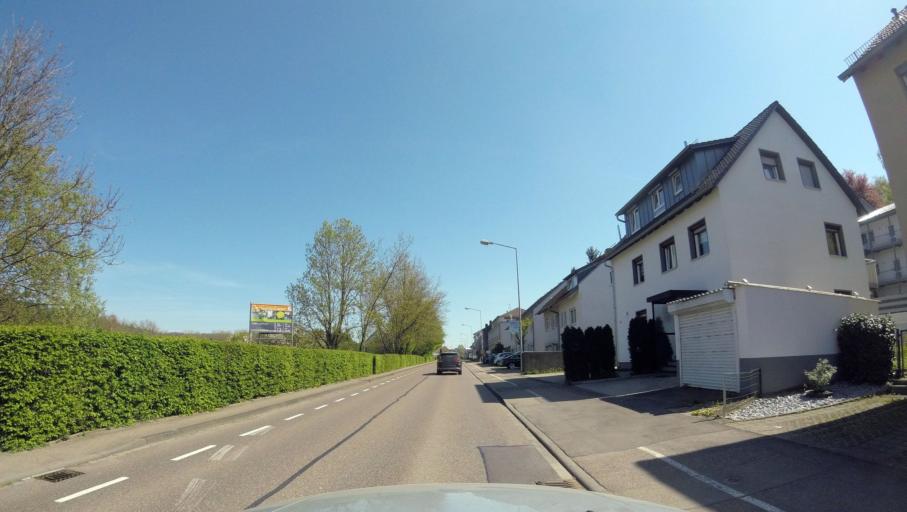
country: DE
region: Baden-Wuerttemberg
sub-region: Regierungsbezirk Stuttgart
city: Schwabisch Gmund
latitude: 48.7912
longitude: 9.7789
